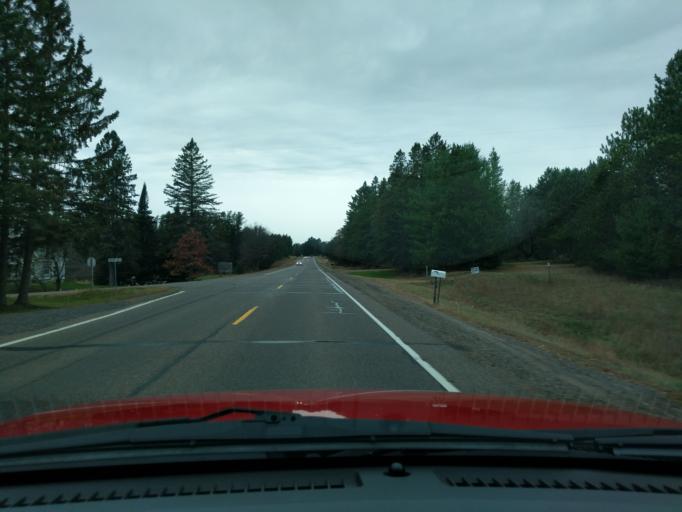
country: US
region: Wisconsin
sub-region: Washburn County
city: Spooner
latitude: 45.8229
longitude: -91.9319
